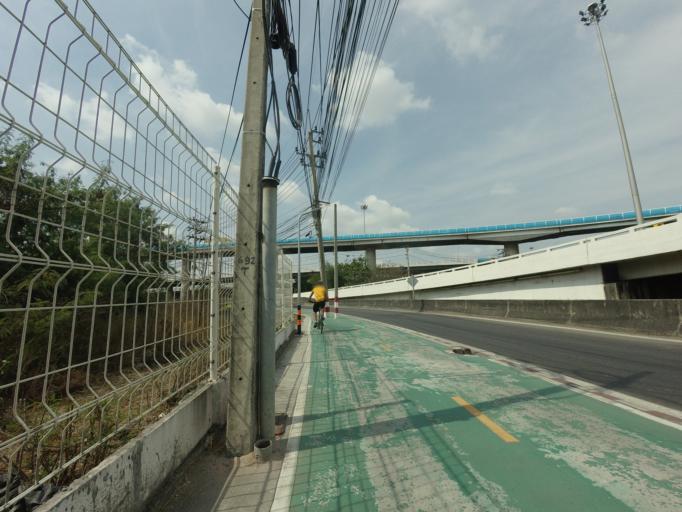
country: TH
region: Bangkok
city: Lat Krabang
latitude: 13.7284
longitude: 100.7461
